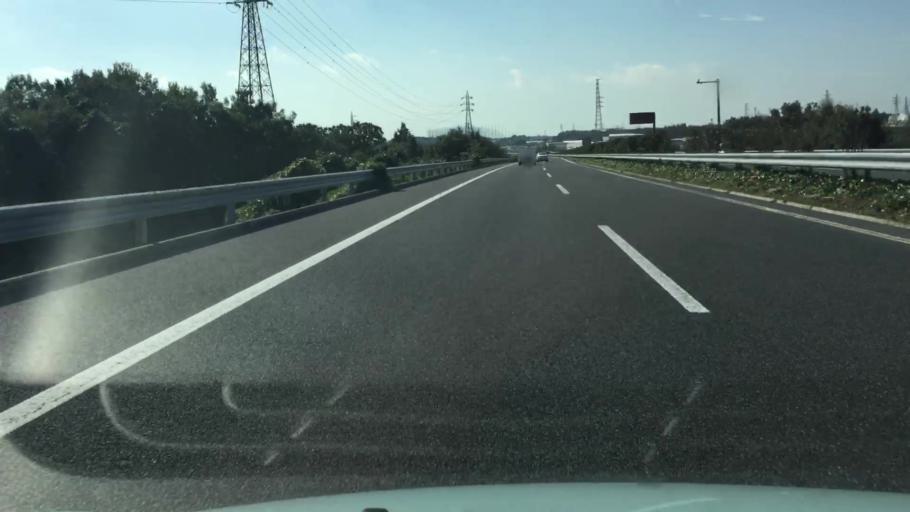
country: JP
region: Tochigi
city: Mooka
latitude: 36.4426
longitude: 139.9697
